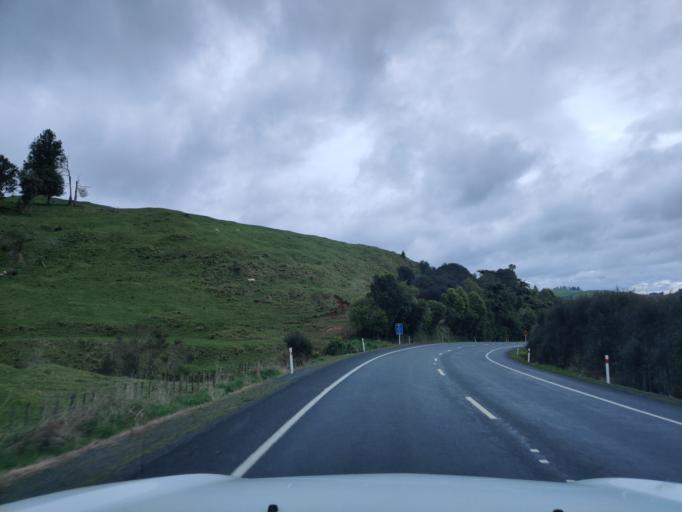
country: NZ
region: Waikato
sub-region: Otorohanga District
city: Otorohanga
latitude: -38.5093
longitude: 175.2055
